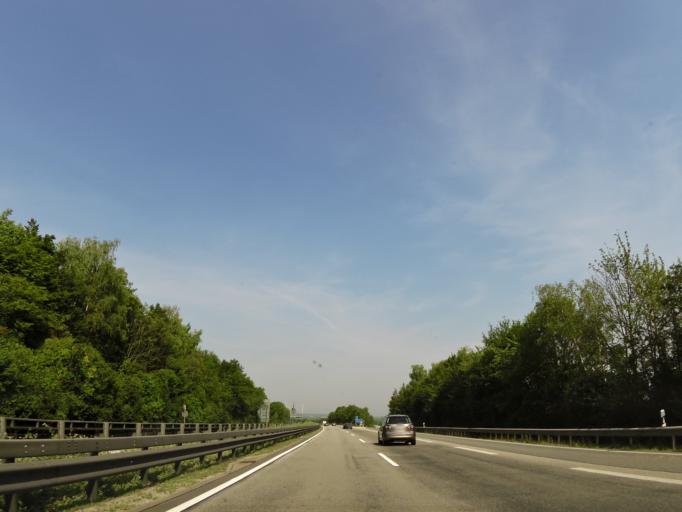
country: DE
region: Rheinland-Pfalz
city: Lonsheim
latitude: 49.7871
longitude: 8.0981
